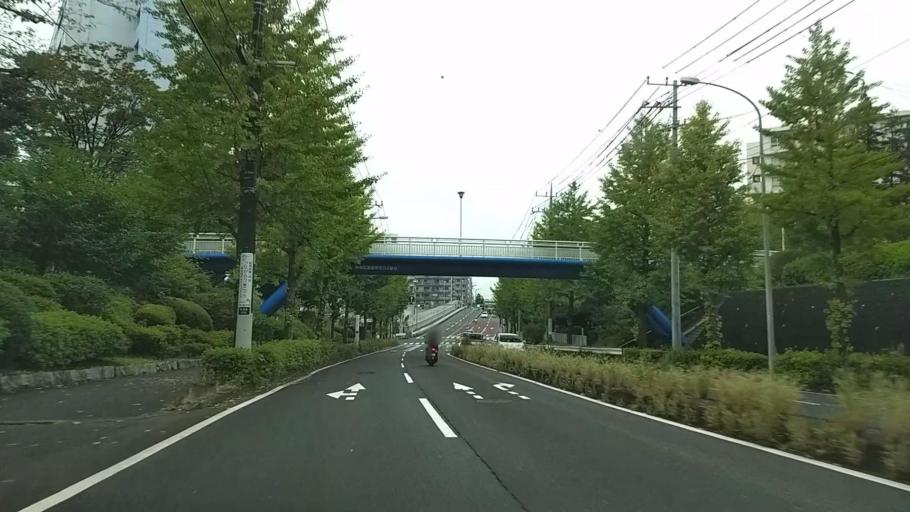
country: JP
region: Kanagawa
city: Kamakura
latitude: 35.3929
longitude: 139.5685
